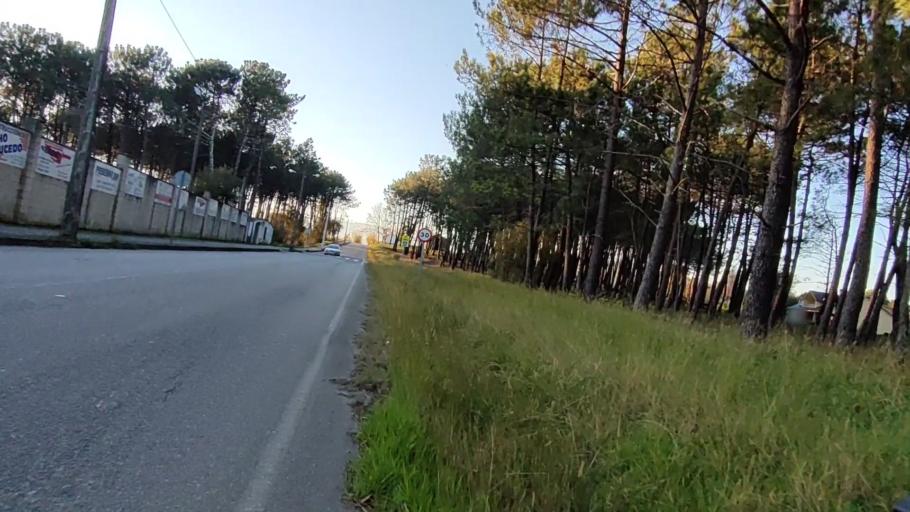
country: ES
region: Galicia
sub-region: Provincia da Coruna
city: Rianxo
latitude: 42.6390
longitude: -8.8563
